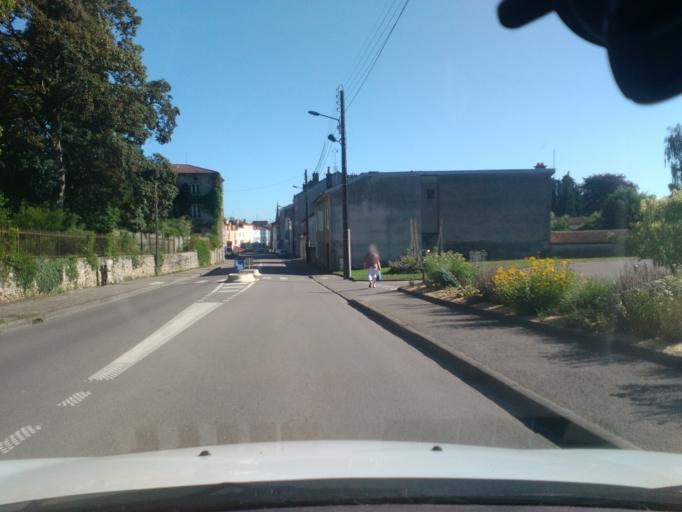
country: FR
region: Lorraine
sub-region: Departement des Vosges
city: Mirecourt
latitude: 48.2954
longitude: 6.1335
